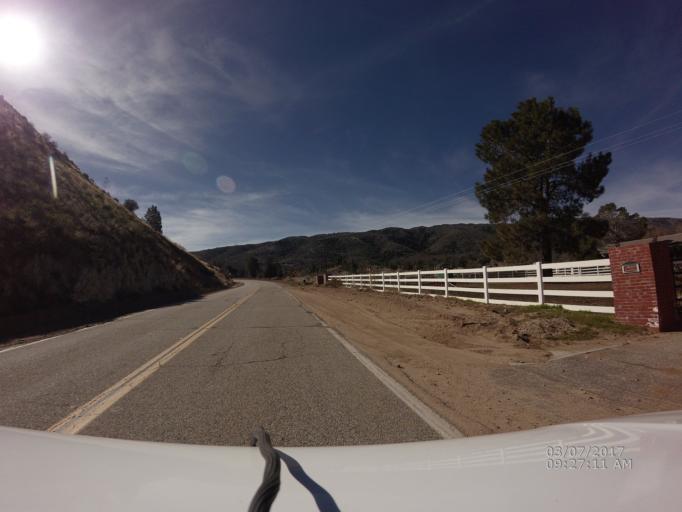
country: US
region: California
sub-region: Los Angeles County
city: Green Valley
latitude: 34.7383
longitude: -118.5997
